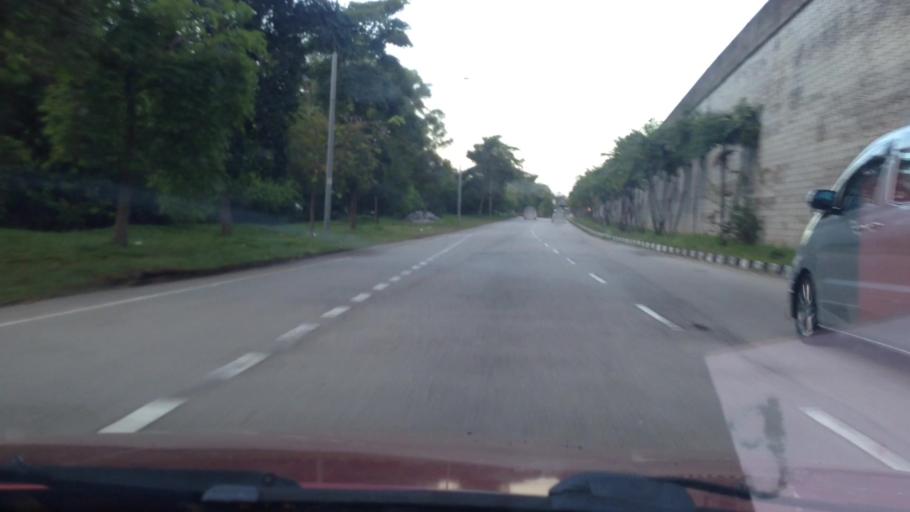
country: MY
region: Selangor
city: Shah Alam
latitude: 3.0998
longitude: 101.5480
